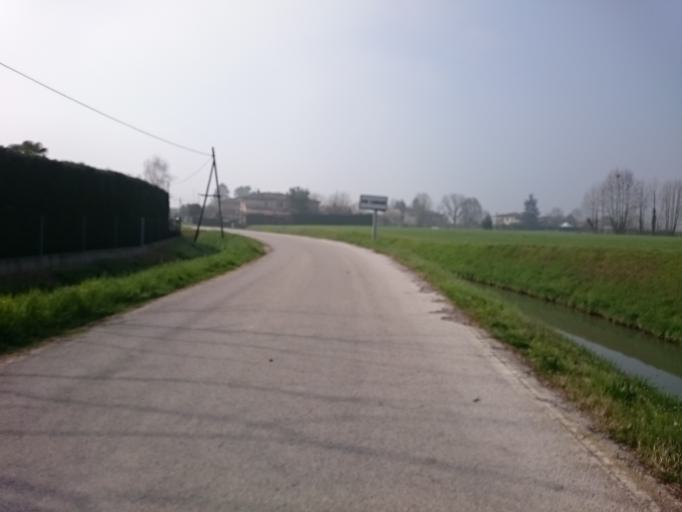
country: IT
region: Veneto
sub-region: Provincia di Padova
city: Due Carrare
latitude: 45.2853
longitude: 11.8324
